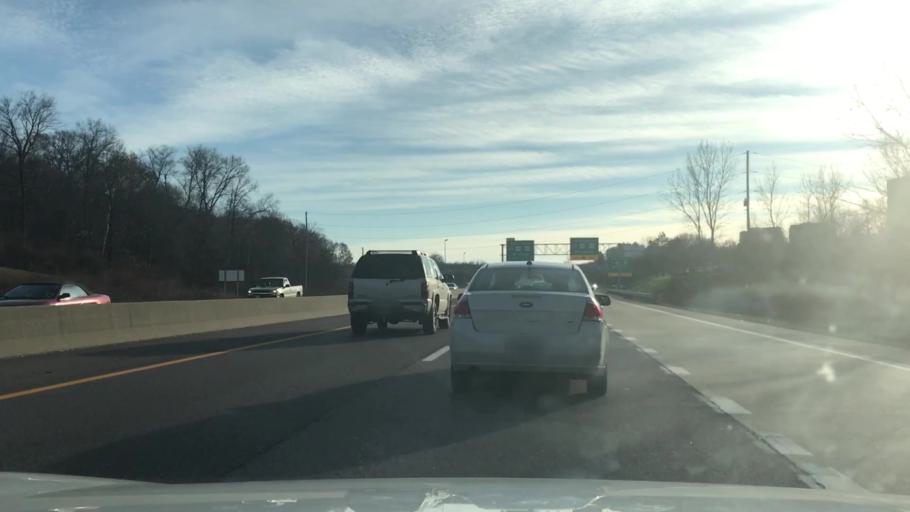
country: US
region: Missouri
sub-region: Saint Louis County
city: Manchester
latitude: 38.6470
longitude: -90.5087
